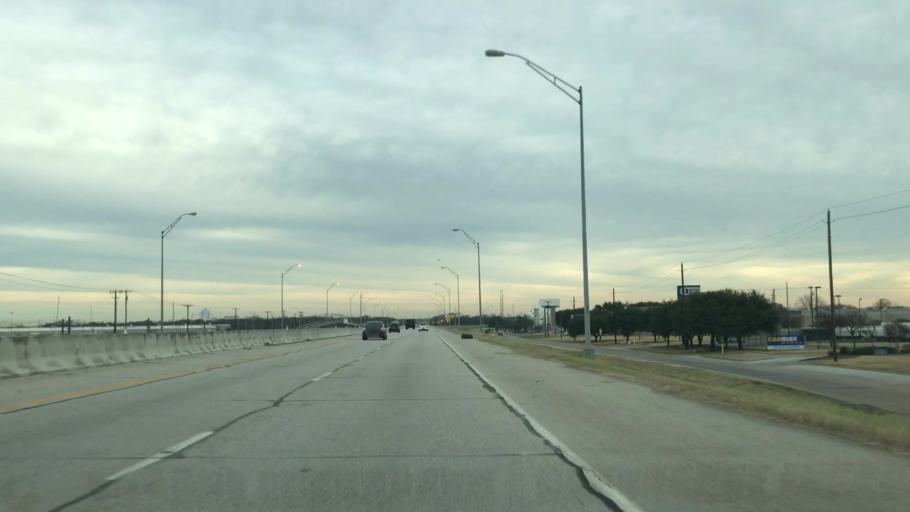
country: US
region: Texas
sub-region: Dallas County
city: Irving
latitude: 32.8412
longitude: -96.9021
